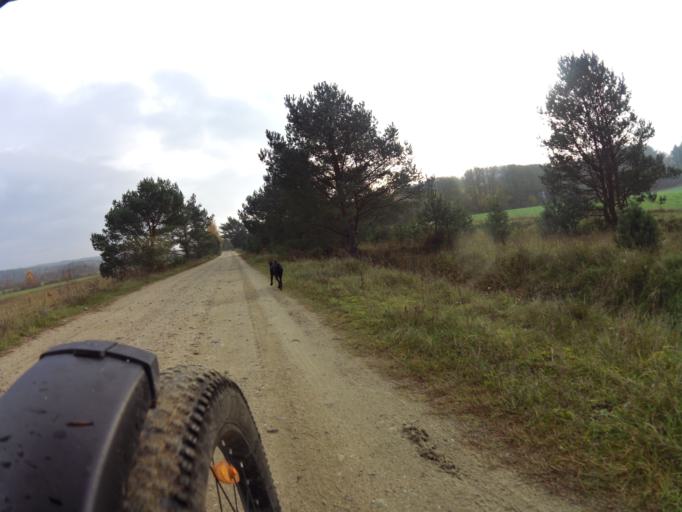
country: PL
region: Pomeranian Voivodeship
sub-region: Powiat wejherowski
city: Gniewino
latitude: 54.7054
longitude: 18.1037
